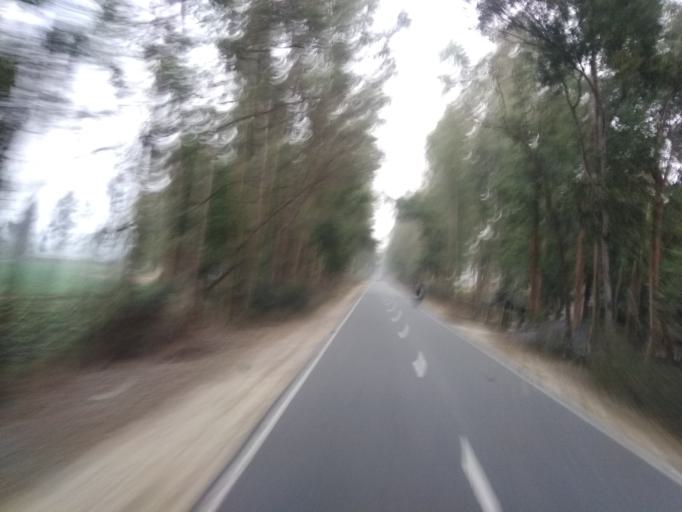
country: BD
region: Rajshahi
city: Bogra
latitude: 24.6672
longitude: 89.2742
